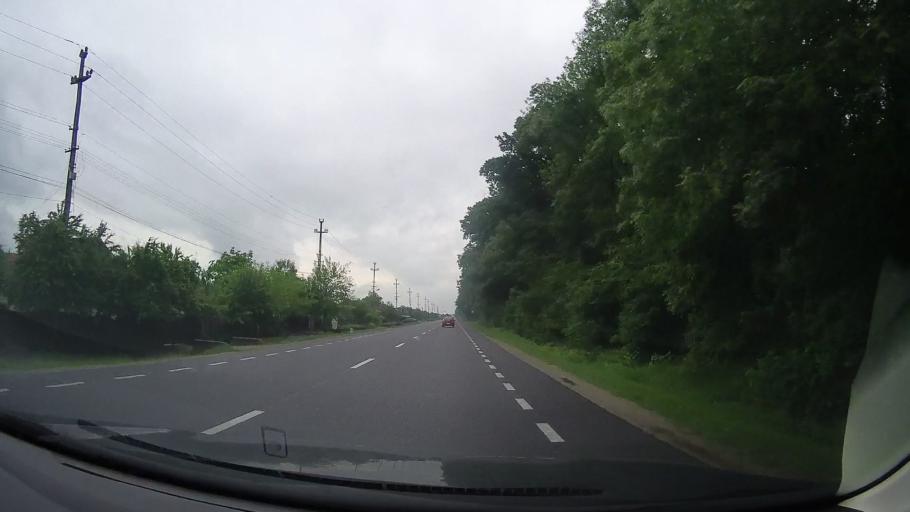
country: RO
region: Mehedinti
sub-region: Oras Strehaia
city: Strehaia
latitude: 44.6103
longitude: 23.2497
